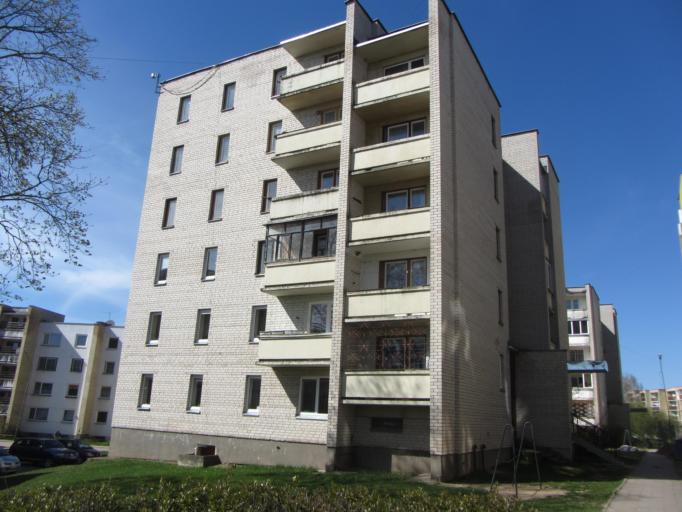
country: LT
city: Zarasai
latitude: 55.7382
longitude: 26.2655
